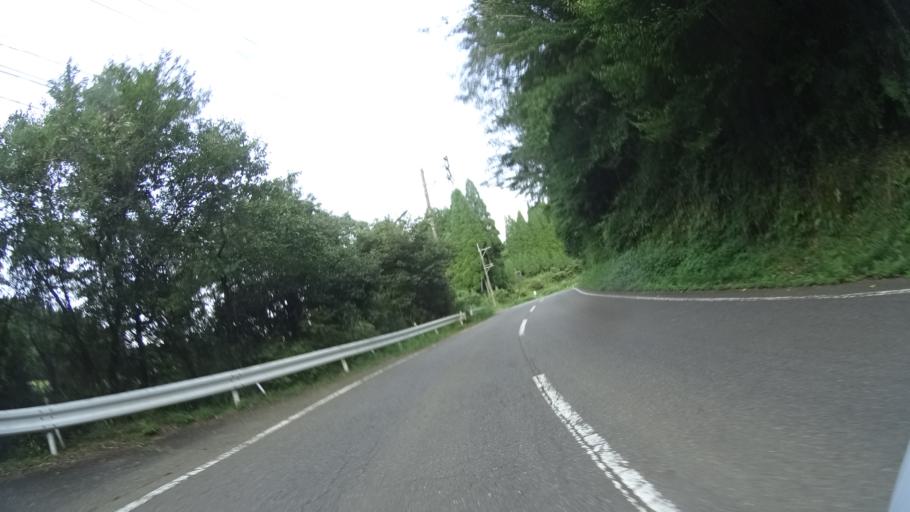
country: JP
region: Kumamoto
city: Ozu
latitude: 32.6887
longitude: 131.0107
